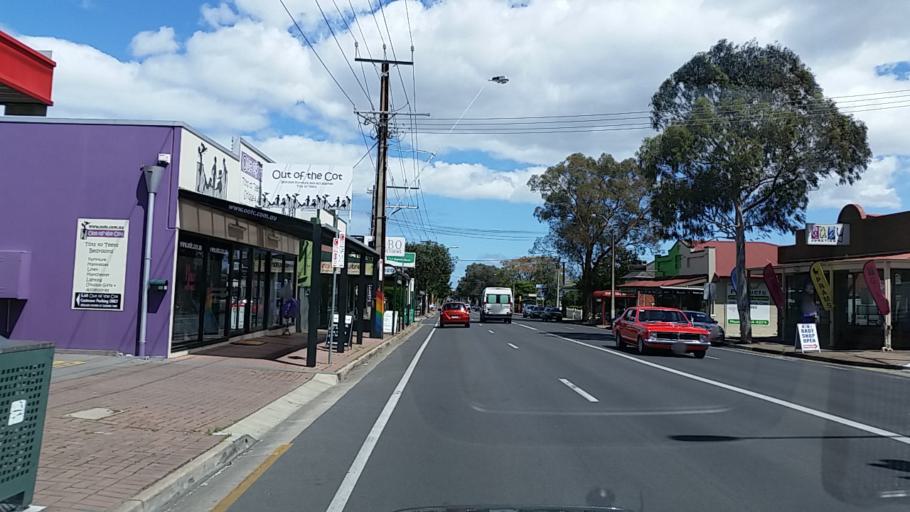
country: AU
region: South Australia
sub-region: Norwood Payneham St Peters
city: Trinity Gardens
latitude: -34.9143
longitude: 138.6512
